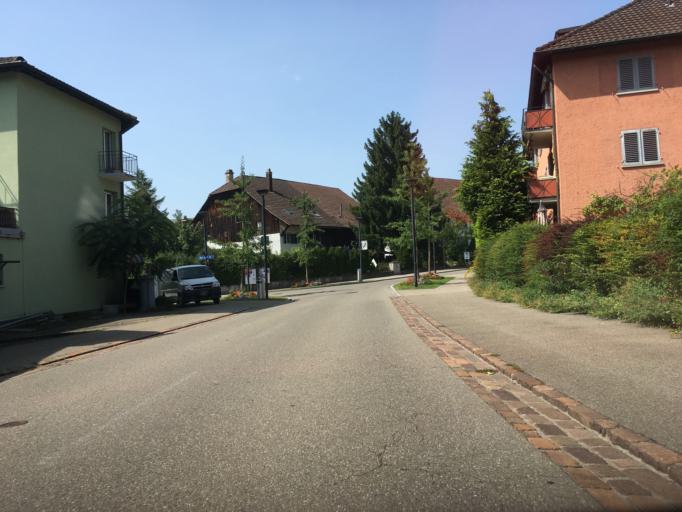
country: CH
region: Zurich
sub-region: Bezirk Buelach
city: Wallisellen / Rieden
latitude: 47.4175
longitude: 8.5988
